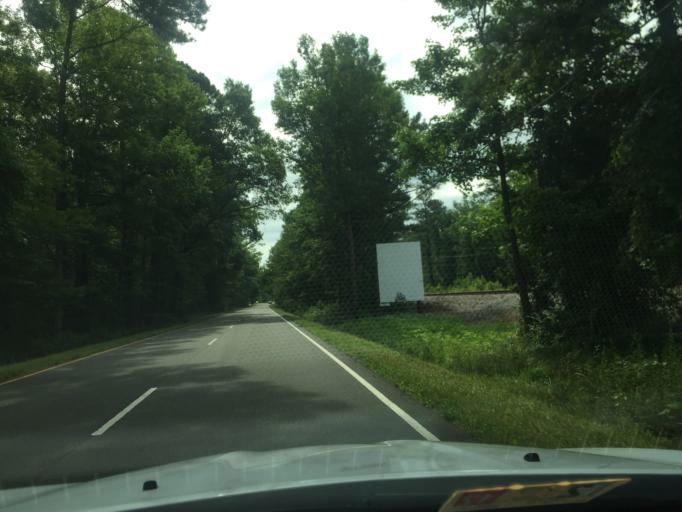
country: US
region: Virginia
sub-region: Charles City County
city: Charles City
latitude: 37.4480
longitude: -77.0679
